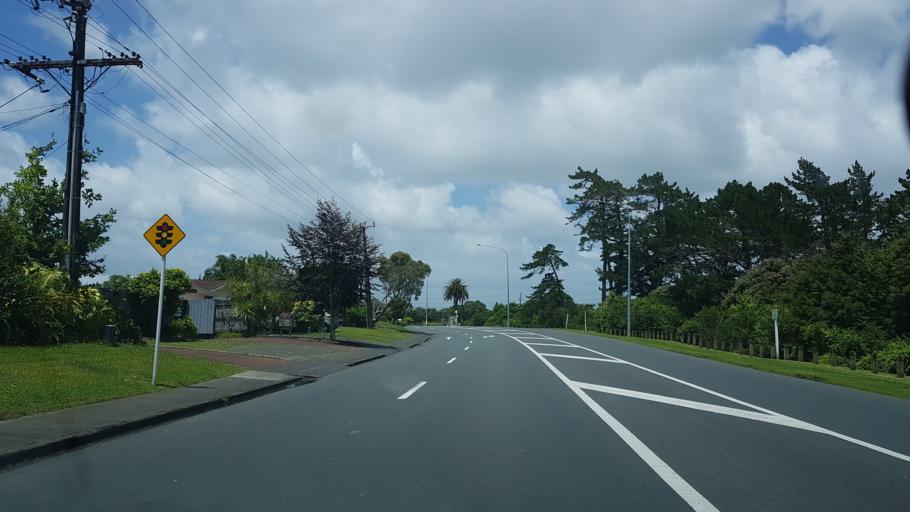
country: NZ
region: Auckland
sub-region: Auckland
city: North Shore
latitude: -36.7971
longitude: 174.7235
